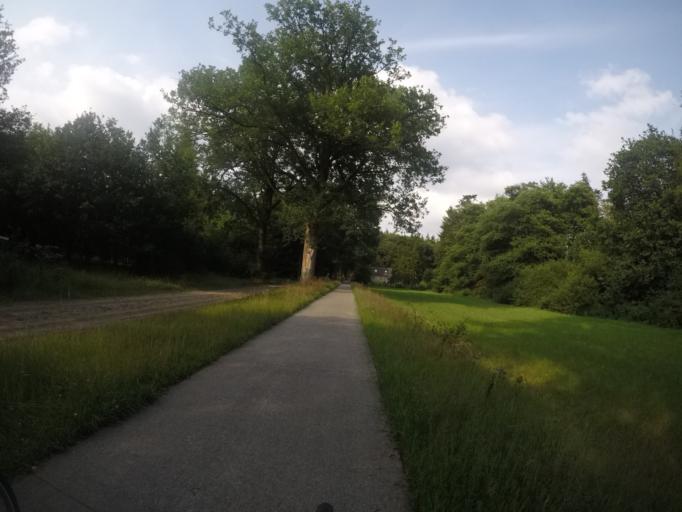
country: NL
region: Friesland
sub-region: Gemeente Weststellingwerf
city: Noordwolde
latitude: 52.8922
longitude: 6.2231
